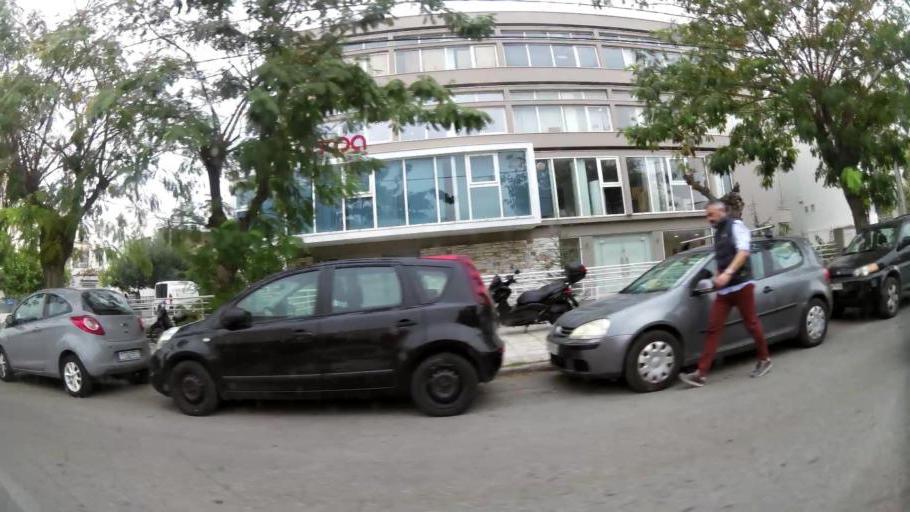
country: GR
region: Attica
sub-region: Nomarchia Athinas
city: Peristeri
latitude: 38.0078
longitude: 23.7067
